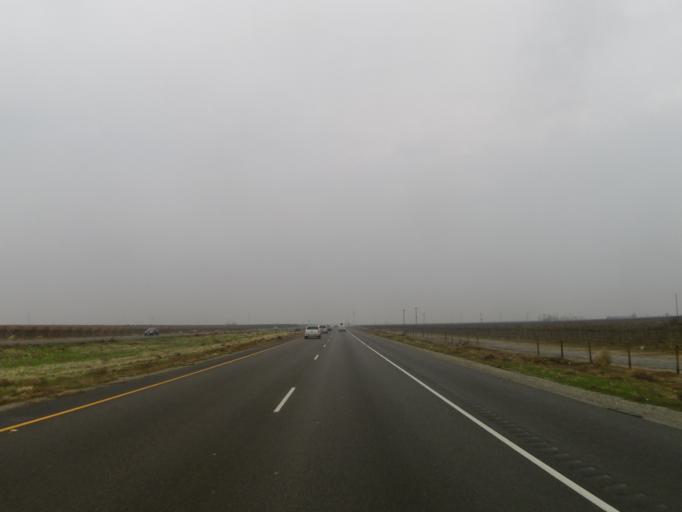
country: US
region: California
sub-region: Kern County
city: Weedpatch
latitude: 35.0391
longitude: -118.9787
